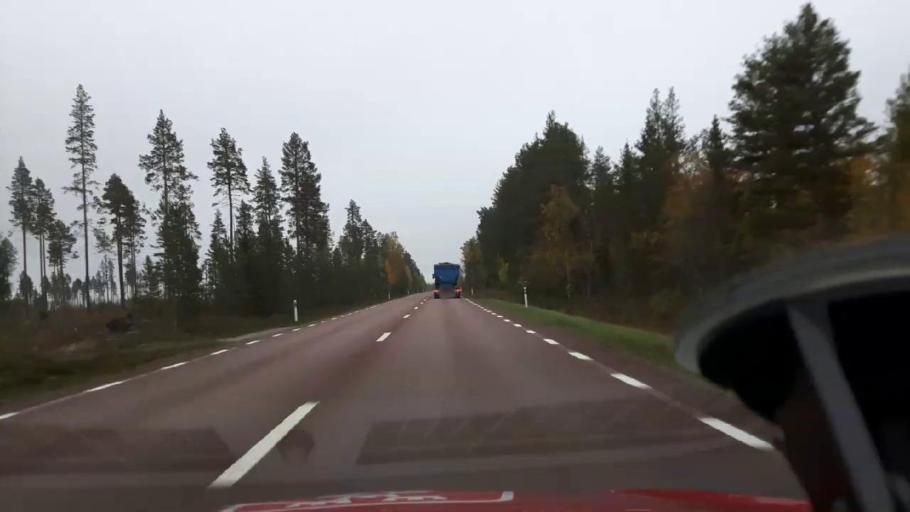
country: SE
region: Jaemtland
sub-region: Bergs Kommun
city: Hoverberg
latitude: 62.5985
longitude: 14.4194
